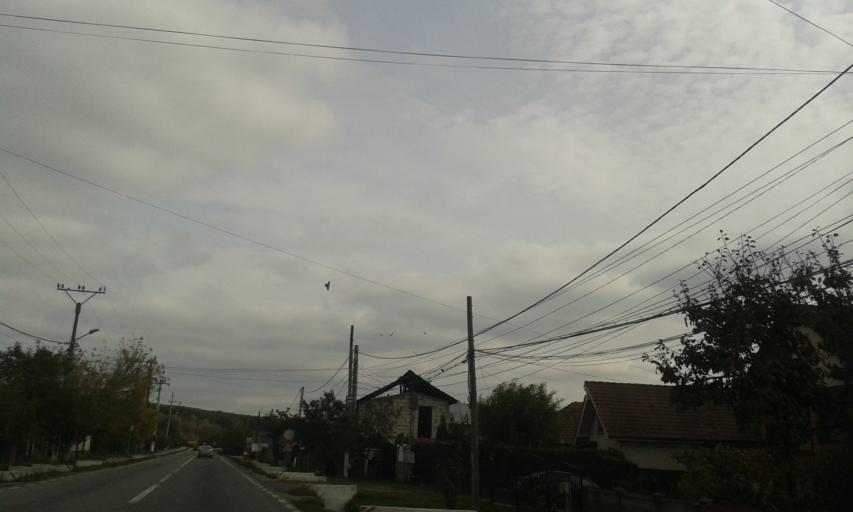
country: RO
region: Gorj
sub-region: Comuna Turcinesti
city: Turcinesti
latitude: 45.0424
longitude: 23.3413
